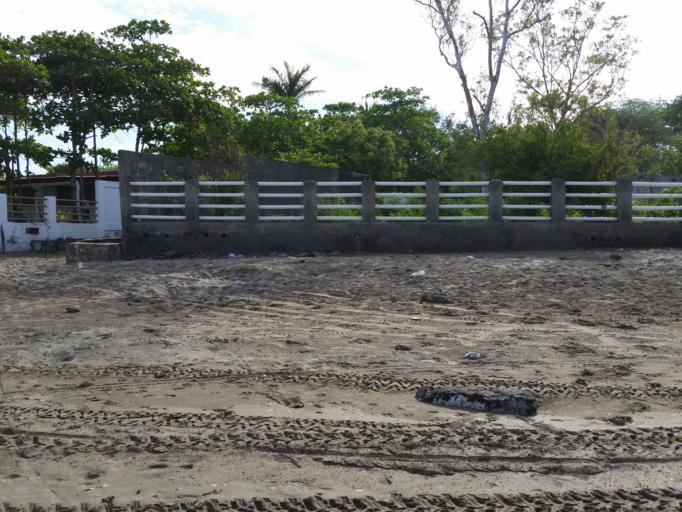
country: NI
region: Managua
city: Masachapa
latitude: 11.7806
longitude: -86.5189
